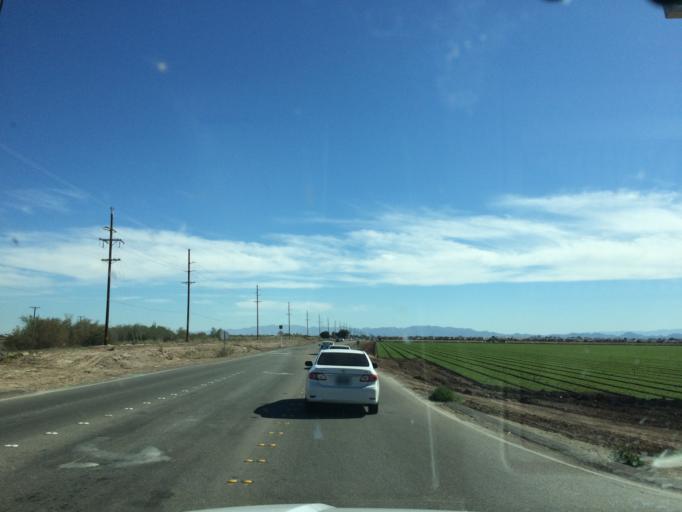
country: US
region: California
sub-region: Imperial County
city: Heber
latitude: 32.7524
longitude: -115.5350
